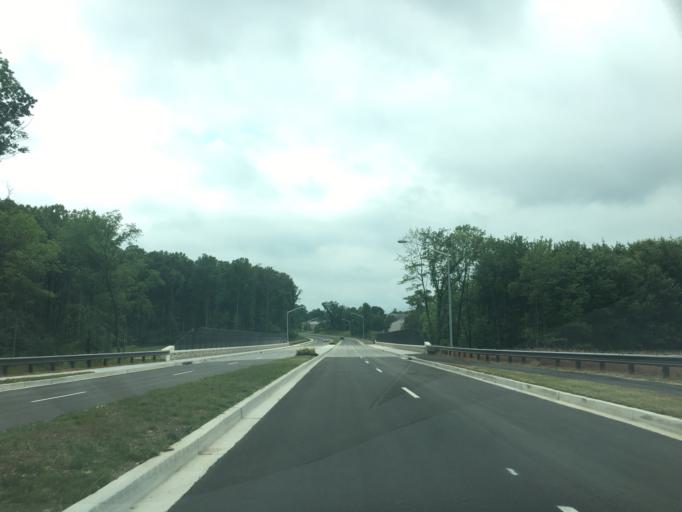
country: US
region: Maryland
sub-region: Baltimore County
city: Randallstown
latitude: 39.3828
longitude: -76.8088
